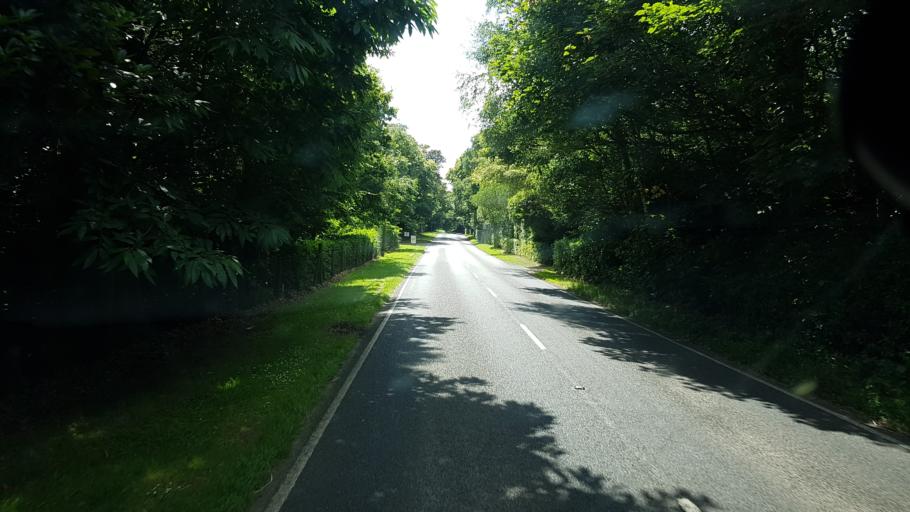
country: GB
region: England
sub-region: West Sussex
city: Broadfield
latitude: 51.0635
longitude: -0.1803
